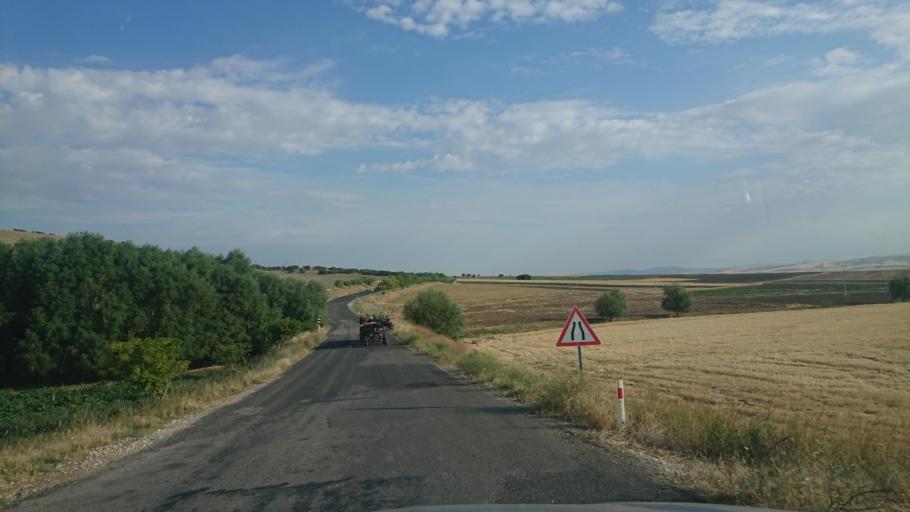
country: TR
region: Aksaray
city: Ortakoy
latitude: 38.7992
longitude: 34.0648
